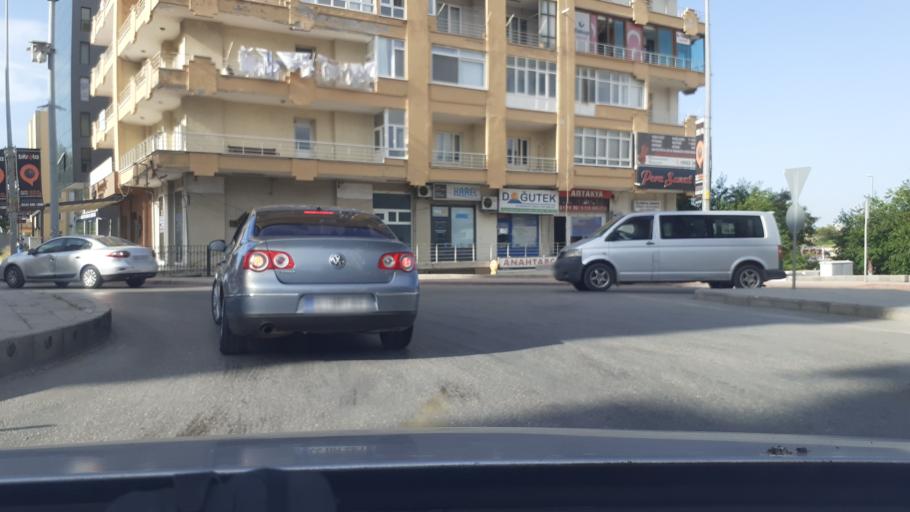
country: TR
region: Hatay
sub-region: Antakya Ilcesi
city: Antakya
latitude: 36.2191
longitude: 36.1617
